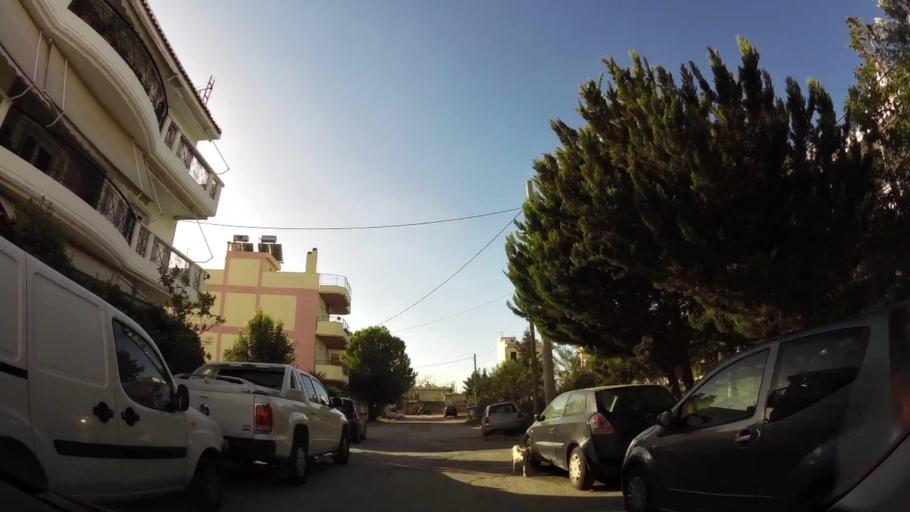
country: GR
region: Attica
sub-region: Nomarchia Anatolikis Attikis
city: Acharnes
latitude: 38.0737
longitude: 23.7446
